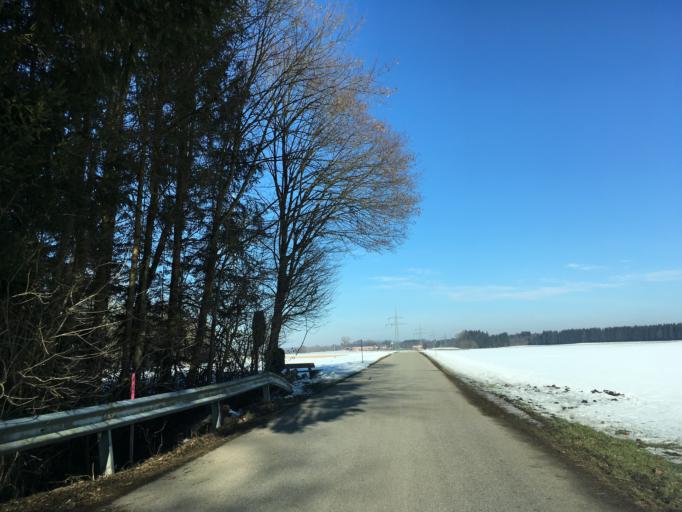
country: DE
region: Bavaria
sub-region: Upper Bavaria
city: Vogtareuth
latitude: 47.9510
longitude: 12.1731
